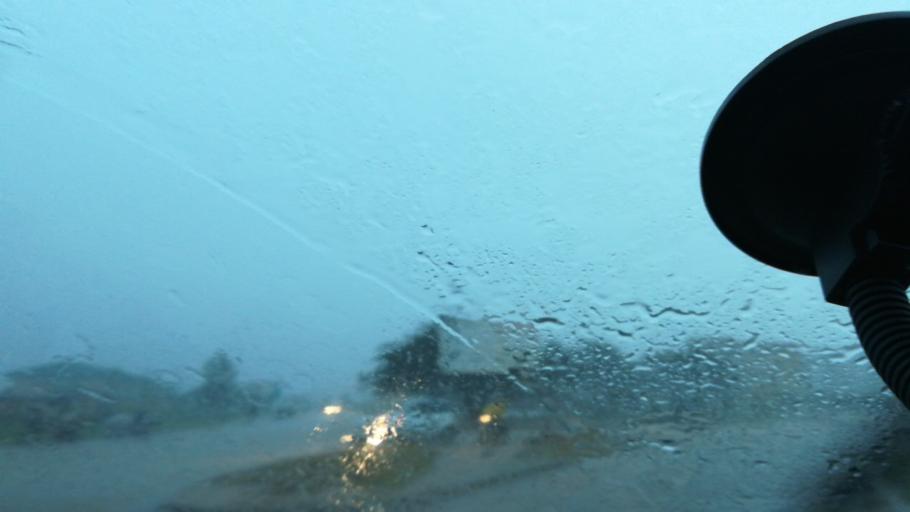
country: CD
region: Katanga
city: Lubumbashi
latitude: -11.5921
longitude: 27.4981
